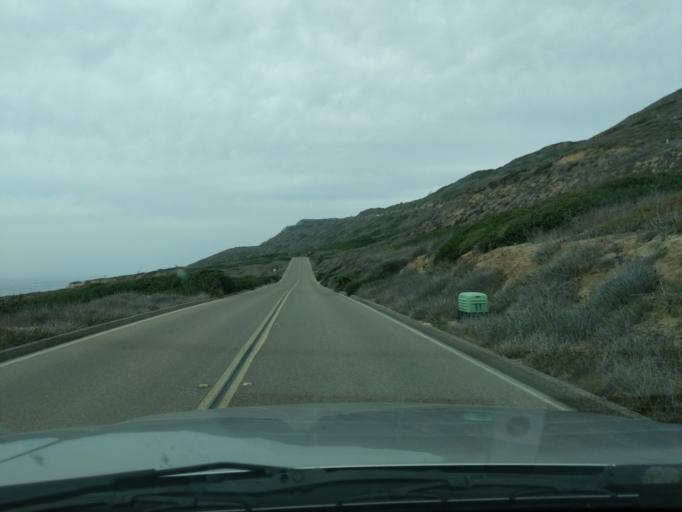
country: US
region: California
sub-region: San Diego County
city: Coronado
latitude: 32.6689
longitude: -117.2435
